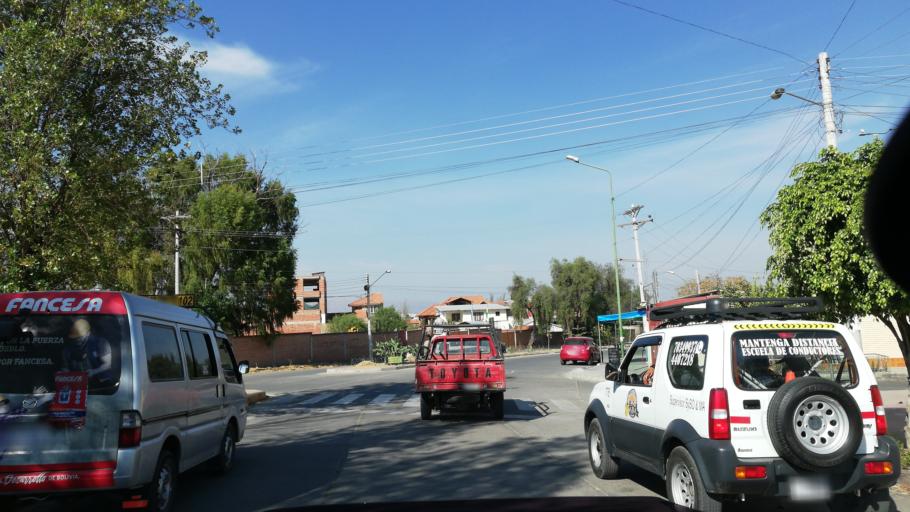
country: BO
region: Cochabamba
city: Cochabamba
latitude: -17.3600
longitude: -66.1868
